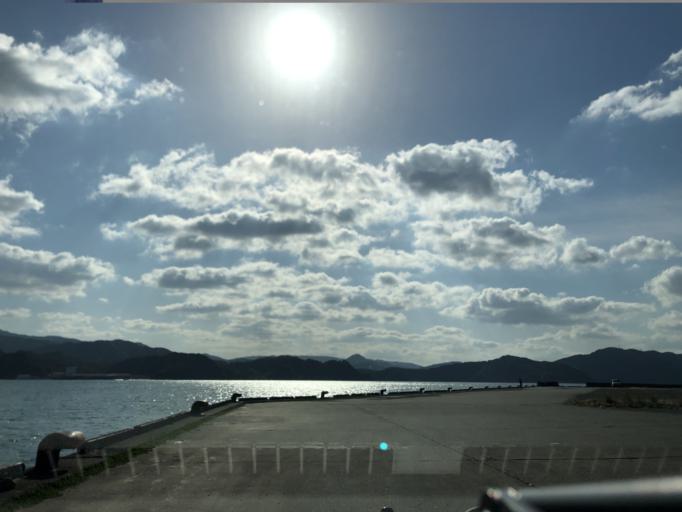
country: JP
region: Kochi
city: Sukumo
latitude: 32.9166
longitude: 132.7050
